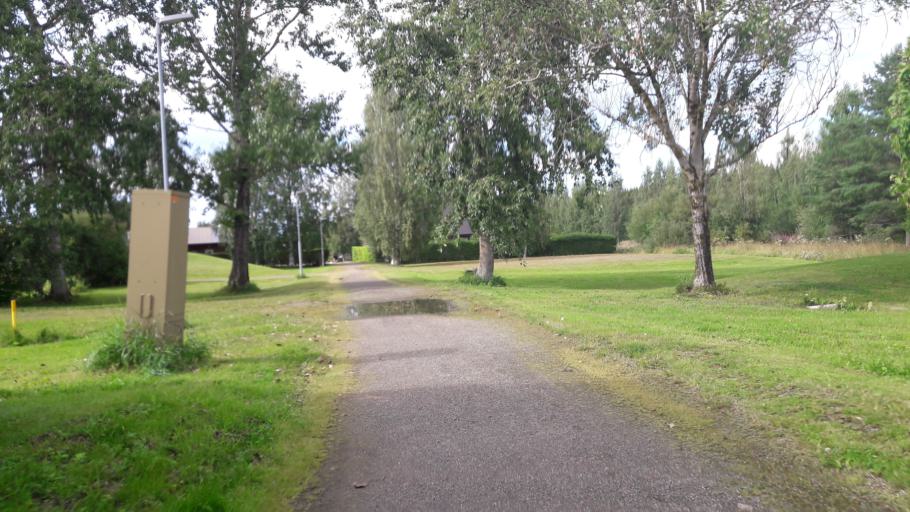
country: FI
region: North Karelia
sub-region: Joensuu
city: Joensuu
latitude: 62.5786
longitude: 29.8125
